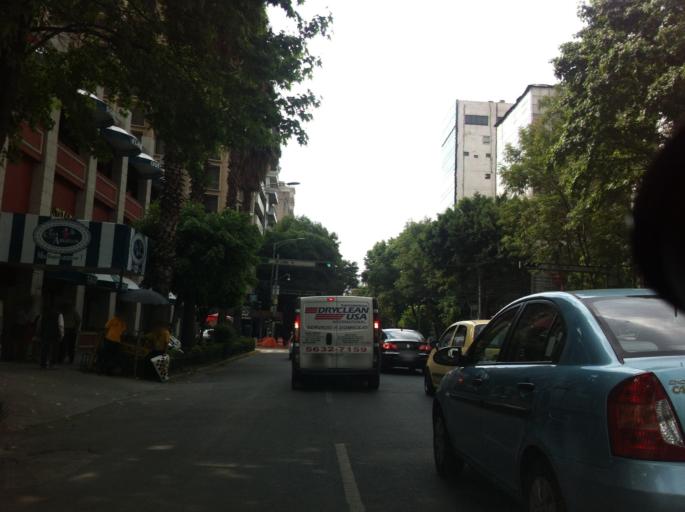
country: MX
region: Mexico City
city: Cuauhtemoc
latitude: 19.4283
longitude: -99.1683
